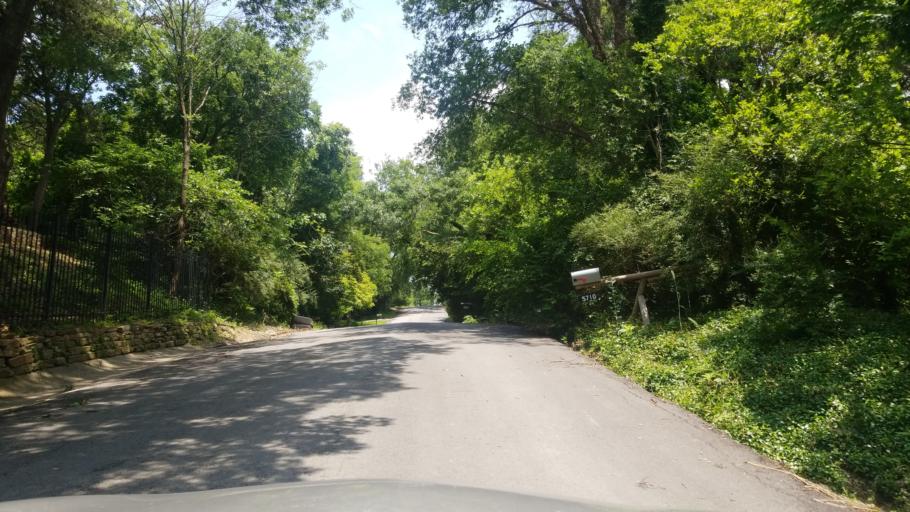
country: US
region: Texas
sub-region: Dallas County
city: Duncanville
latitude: 32.6772
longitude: -96.9215
